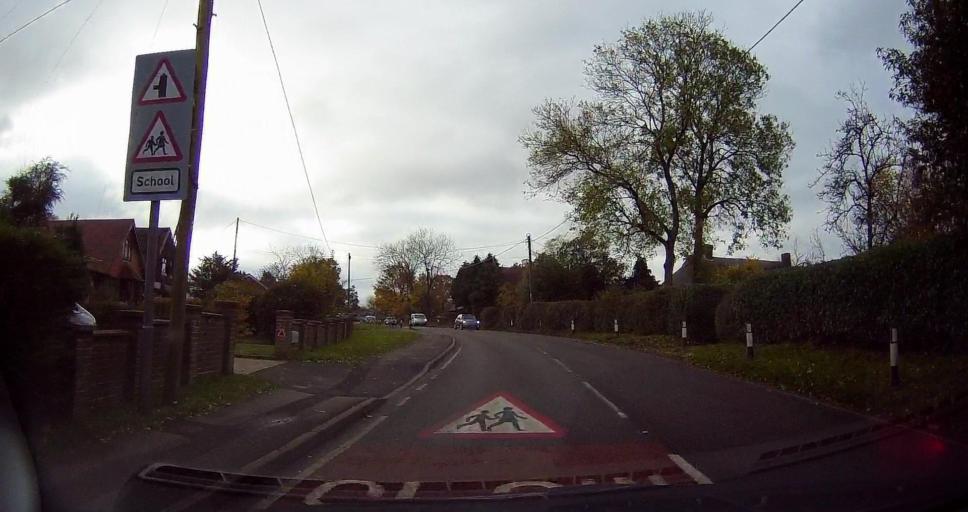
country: GB
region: England
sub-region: Kent
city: Meopham
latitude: 51.3451
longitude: 0.3476
